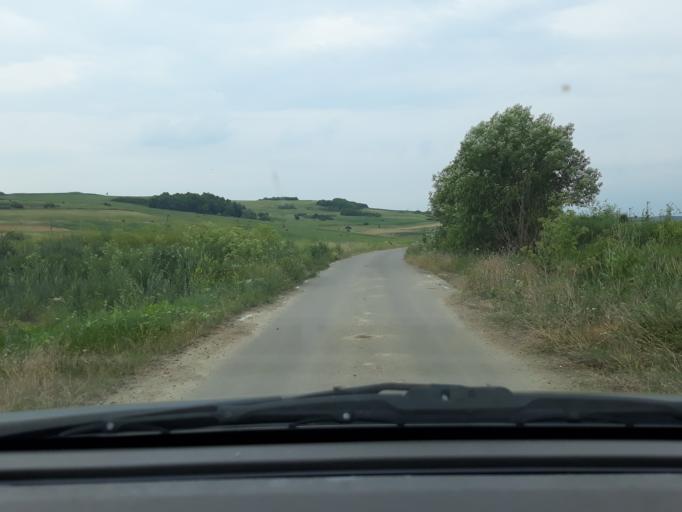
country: RO
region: Salaj
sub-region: Comuna Dobrin
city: Dobrin
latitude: 47.2859
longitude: 23.0947
